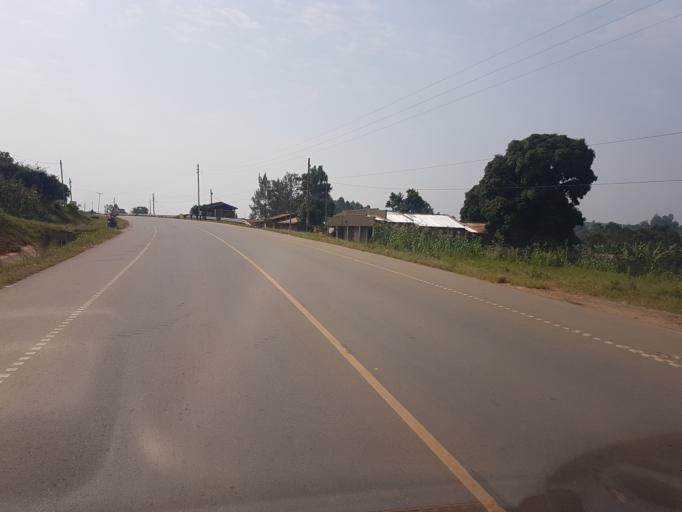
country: UG
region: Western Region
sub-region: Mbarara District
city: Bwizibwera
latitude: -0.6368
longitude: 30.6096
